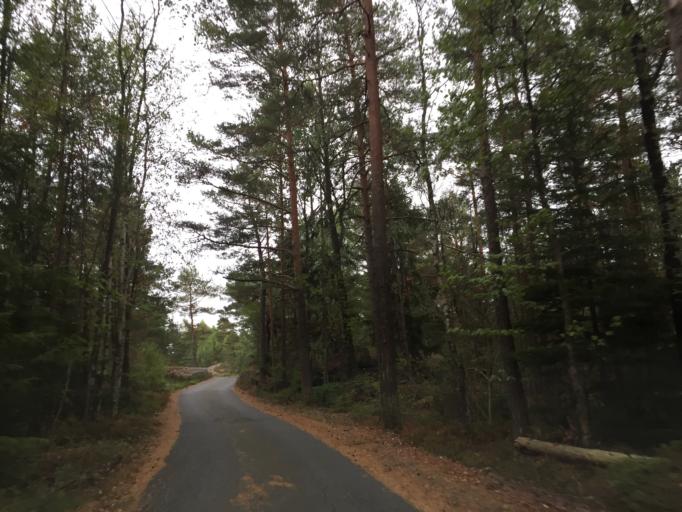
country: NO
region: Ostfold
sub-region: Hvaler
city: Skjaerhalden
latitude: 59.0801
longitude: 11.0038
